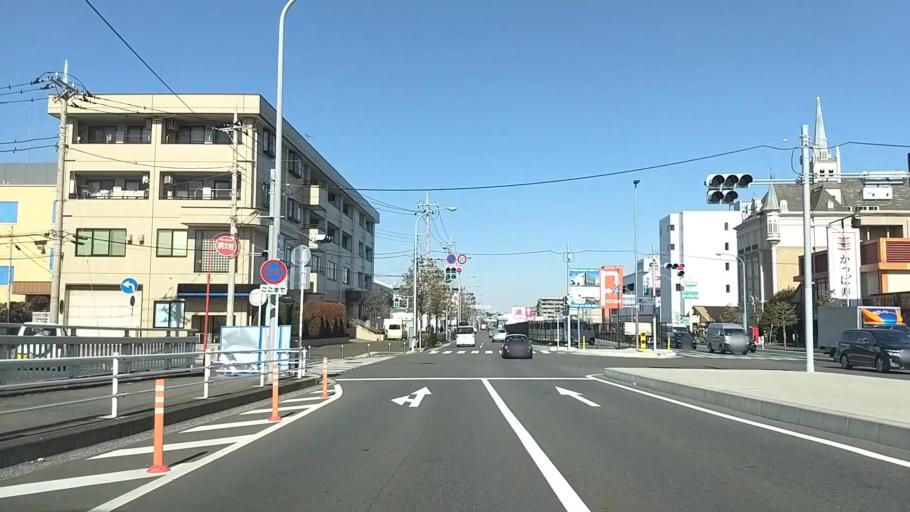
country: JP
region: Kanagawa
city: Yokohama
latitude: 35.5160
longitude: 139.6129
